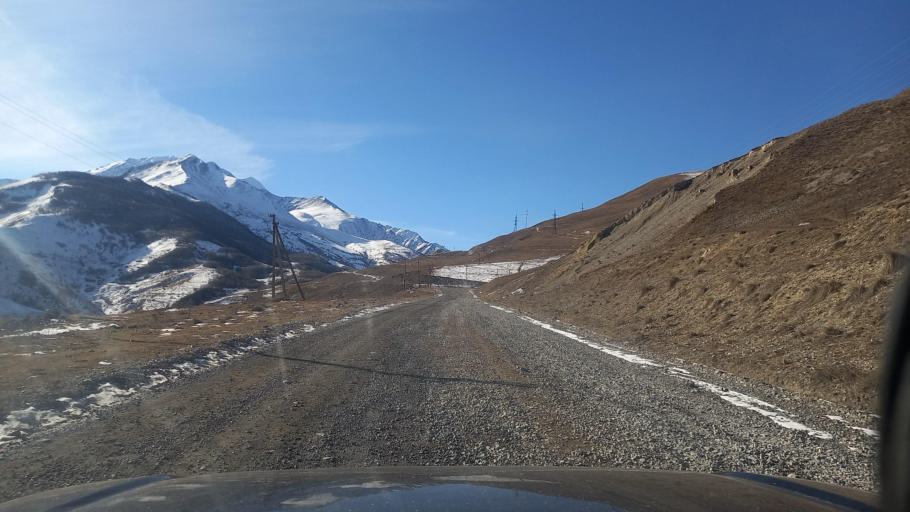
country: RU
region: Ingushetiya
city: Dzhayrakh
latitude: 42.8388
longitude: 44.4963
